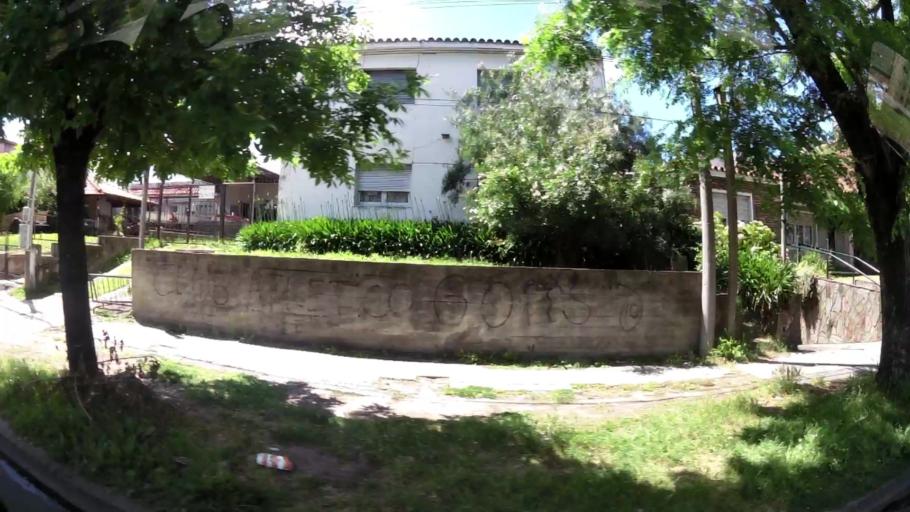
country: UY
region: Montevideo
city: Montevideo
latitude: -34.8544
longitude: -56.1334
